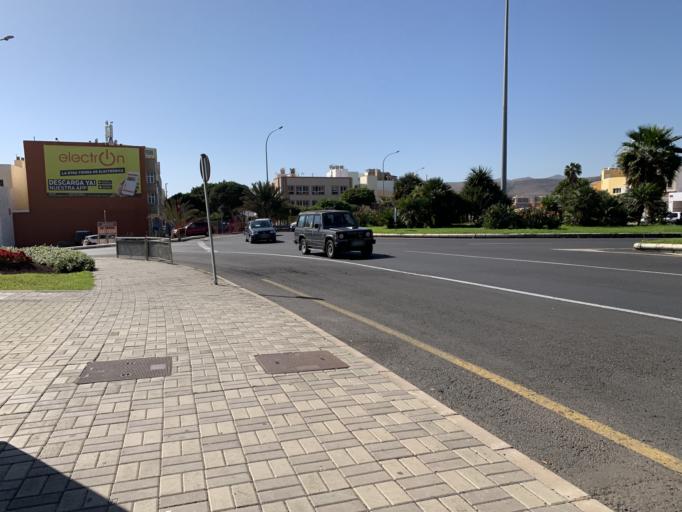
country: ES
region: Canary Islands
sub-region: Provincia de Las Palmas
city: Puerto del Rosario
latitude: 28.4956
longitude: -13.8644
